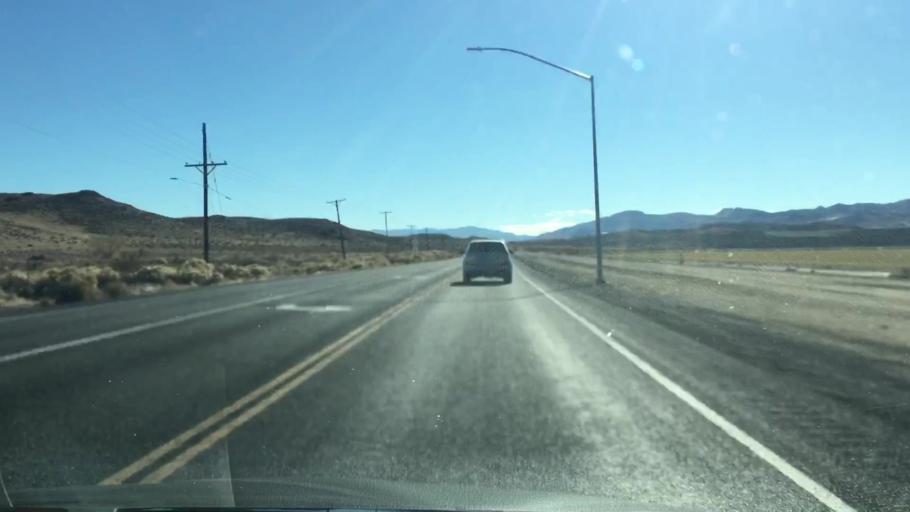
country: US
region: Nevada
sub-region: Lyon County
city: Yerington
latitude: 39.0260
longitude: -119.1816
